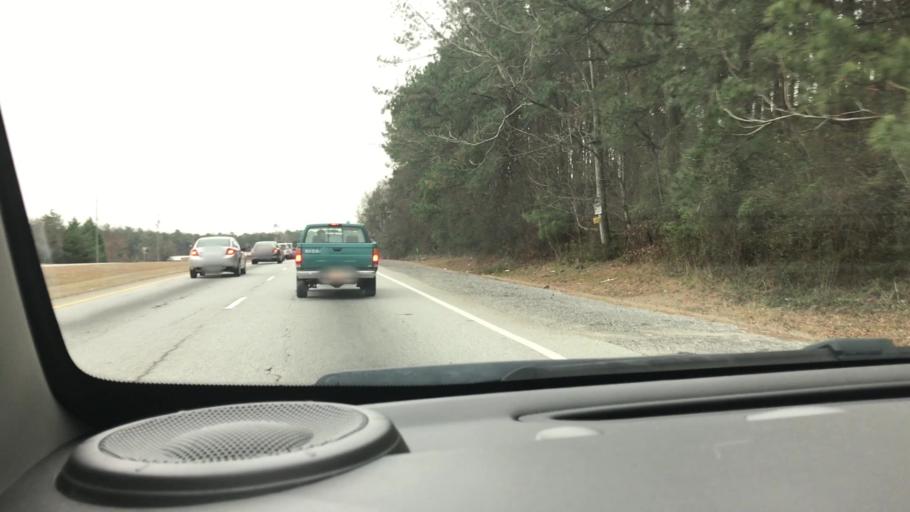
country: US
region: Georgia
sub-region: Clayton County
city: Forest Park
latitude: 33.6214
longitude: -84.4026
